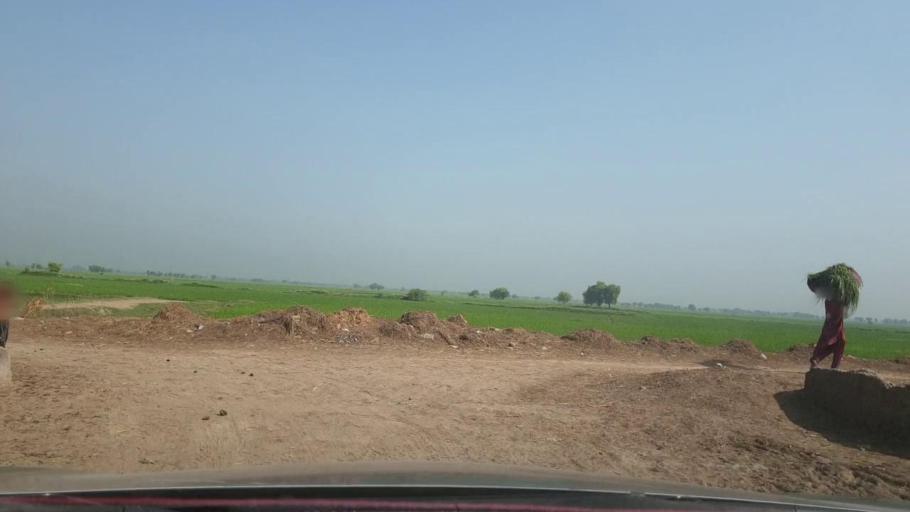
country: PK
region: Sindh
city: Kambar
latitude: 27.6054
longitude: 67.9356
